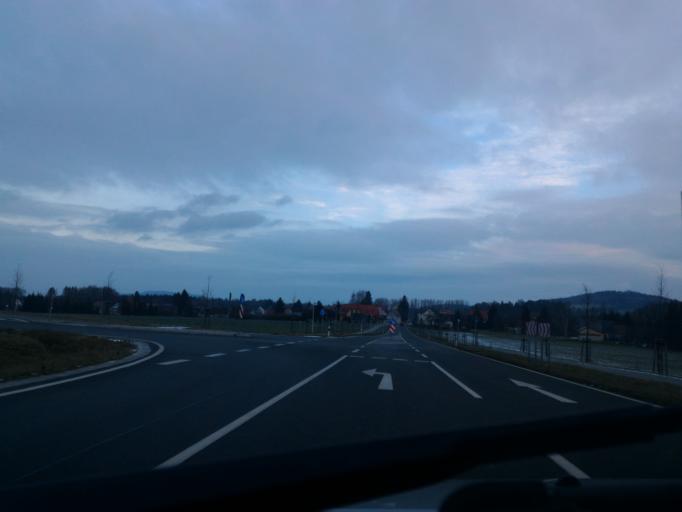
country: DE
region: Saxony
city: Leutersdorf
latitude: 50.9454
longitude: 14.6735
